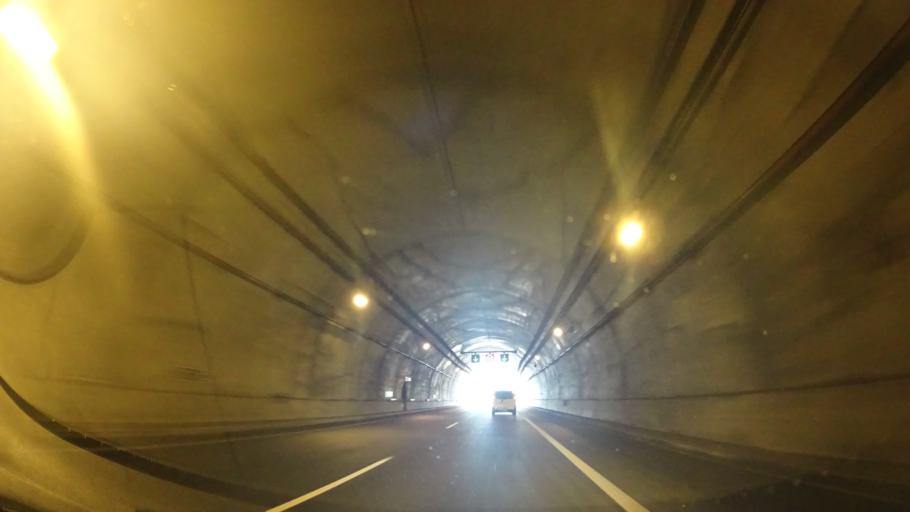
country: ES
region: Asturias
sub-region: Province of Asturias
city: Arriba
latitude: 43.4919
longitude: -5.5316
